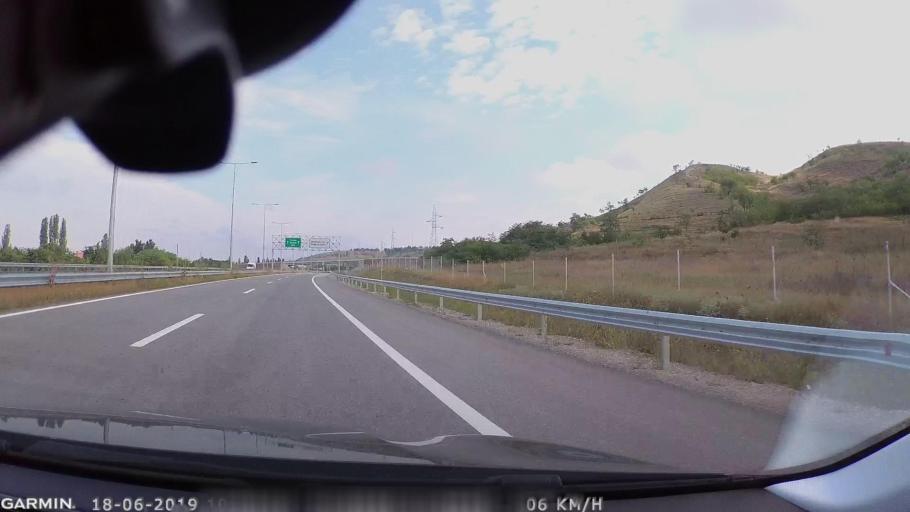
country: MK
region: Sveti Nikole
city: Sveti Nikole
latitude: 41.8532
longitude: 21.9642
